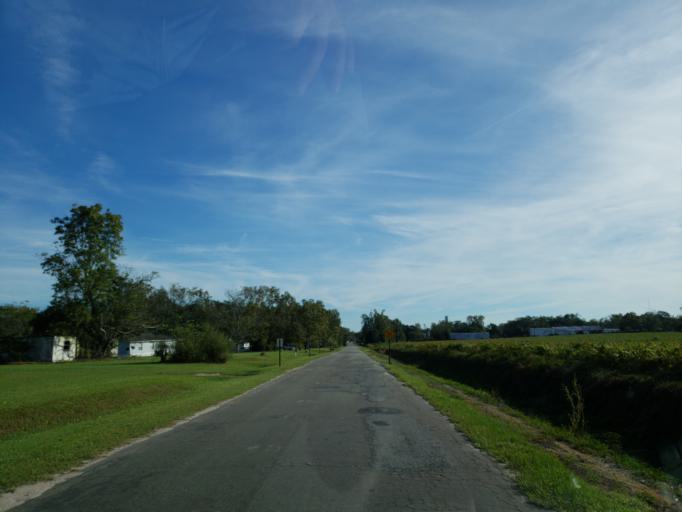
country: US
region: Georgia
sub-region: Dooly County
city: Unadilla
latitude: 32.2021
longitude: -83.7597
